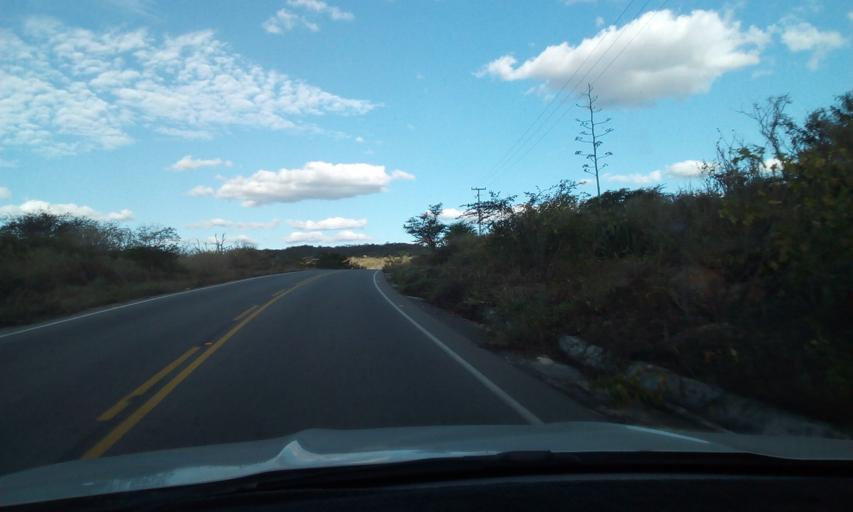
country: BR
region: Paraiba
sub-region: Picui
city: Picui
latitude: -6.5647
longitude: -36.2784
